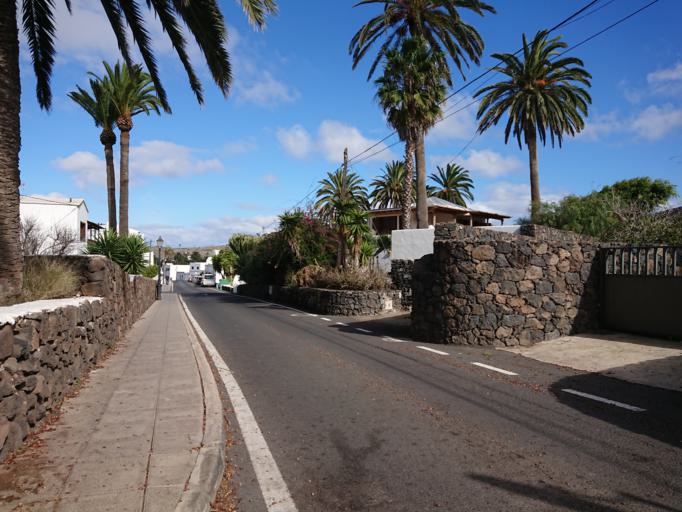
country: ES
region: Canary Islands
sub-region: Provincia de Las Palmas
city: Haria
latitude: 29.1428
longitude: -13.5038
